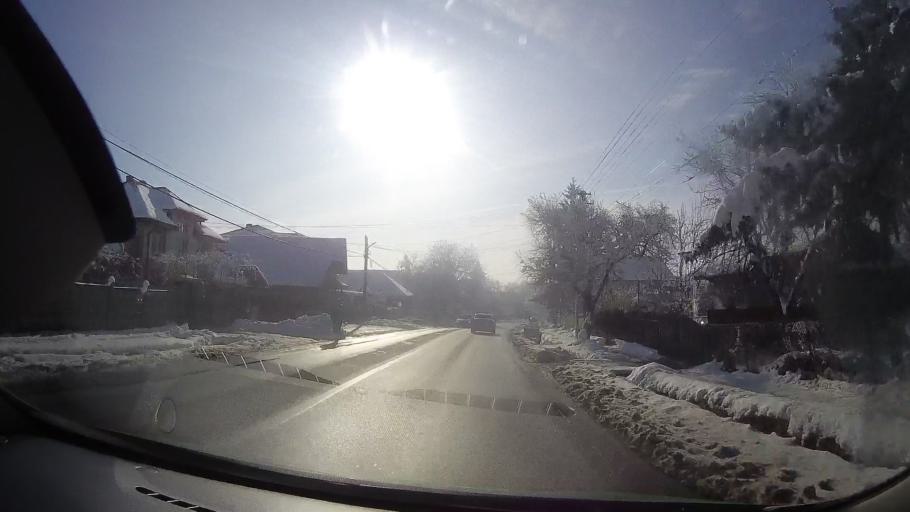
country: RO
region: Iasi
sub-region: Comuna Motca
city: Motca
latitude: 47.2433
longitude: 26.6085
